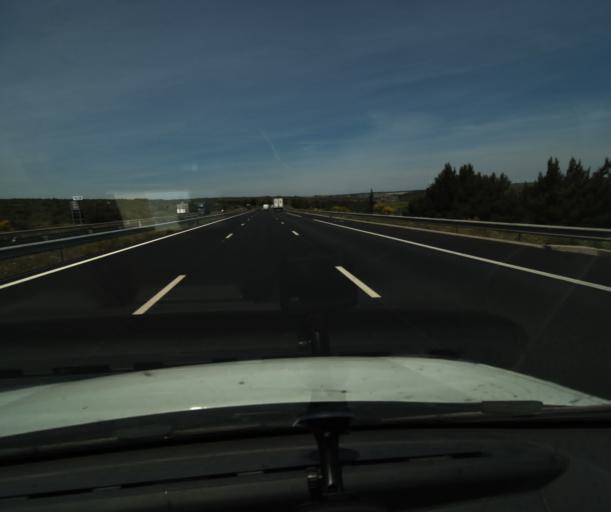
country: FR
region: Languedoc-Roussillon
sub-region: Departement de l'Aude
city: Sigean
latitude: 42.9615
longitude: 2.9692
